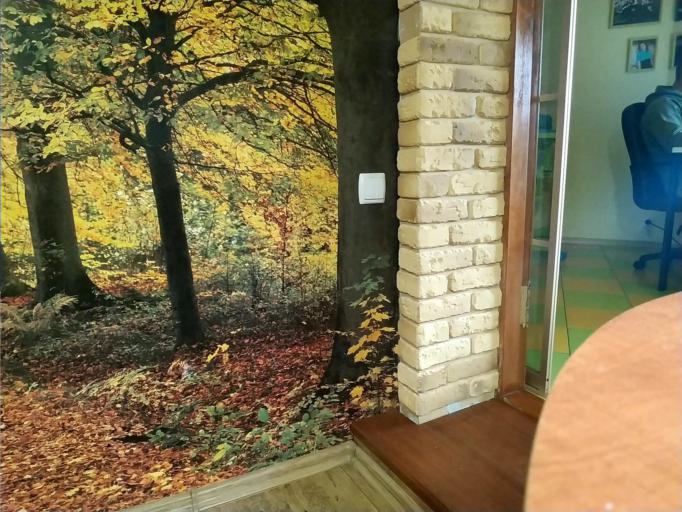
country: RU
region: Smolensk
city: Dorogobuzh
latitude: 54.9801
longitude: 33.2763
